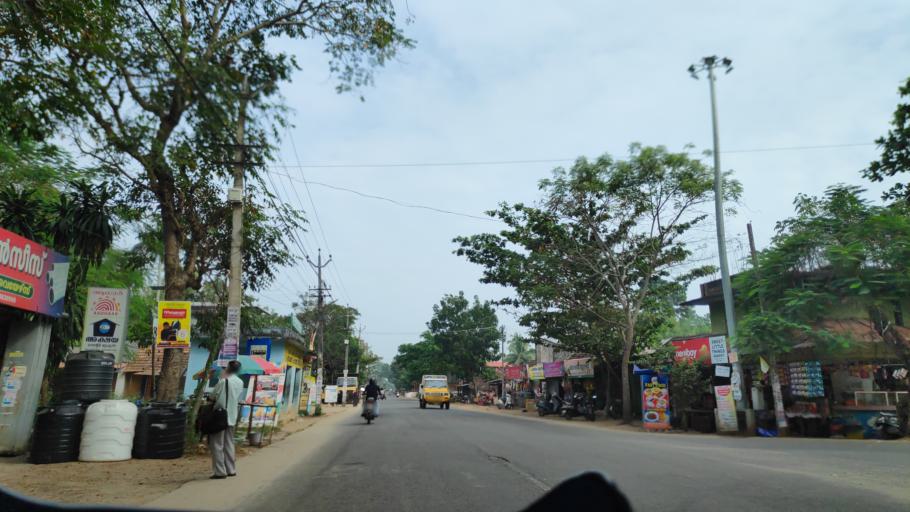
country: IN
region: Kerala
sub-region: Kottayam
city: Vaikam
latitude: 9.7543
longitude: 76.3634
